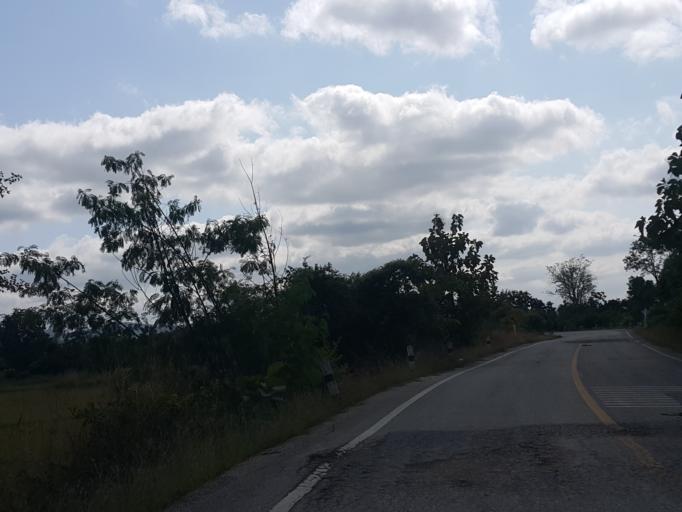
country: TH
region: Lamphun
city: Lamphun
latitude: 18.5423
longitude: 99.0877
